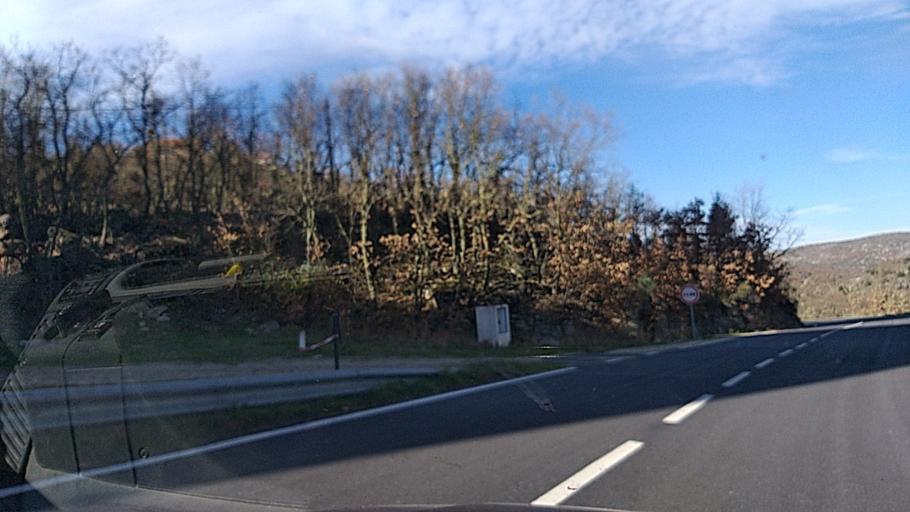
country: ES
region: Castille and Leon
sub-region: Provincia de Salamanca
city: Fuentes de Onoro
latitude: 40.6108
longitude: -6.9213
